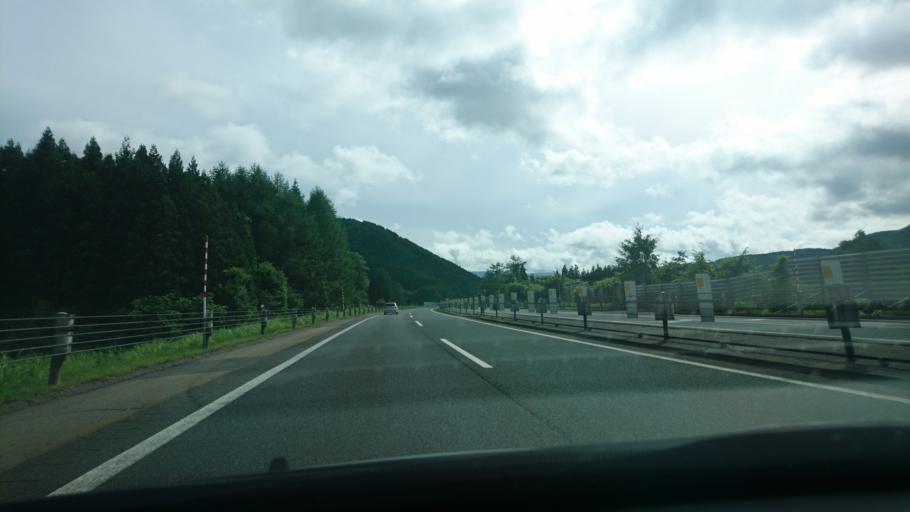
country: JP
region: Akita
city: Hanawa
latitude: 40.0529
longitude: 141.0152
